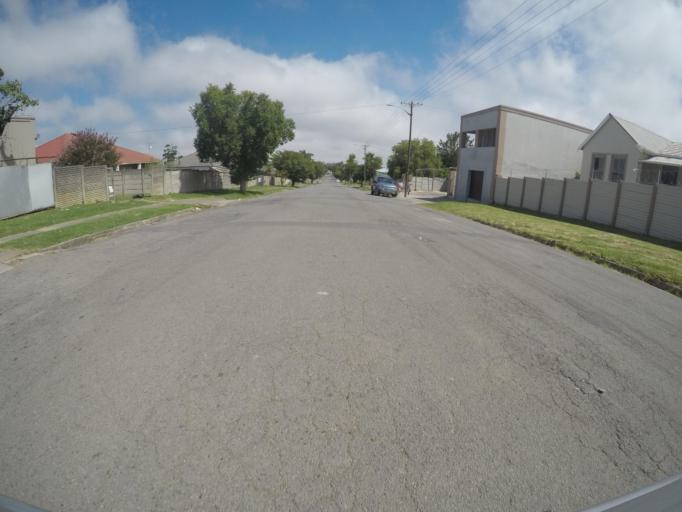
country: ZA
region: Eastern Cape
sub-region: Buffalo City Metropolitan Municipality
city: East London
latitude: -32.9752
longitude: 27.8895
